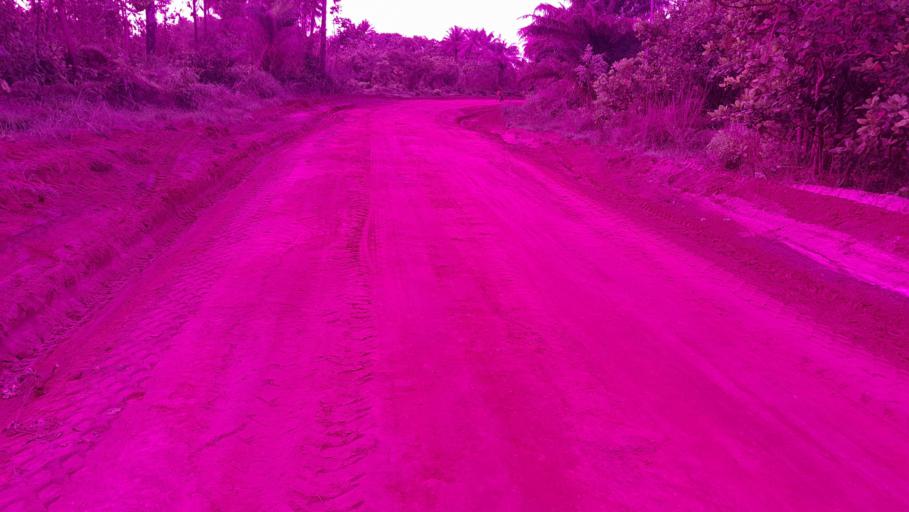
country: GN
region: Boke
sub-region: Boffa
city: Boffa
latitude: 10.0722
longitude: -13.8683
